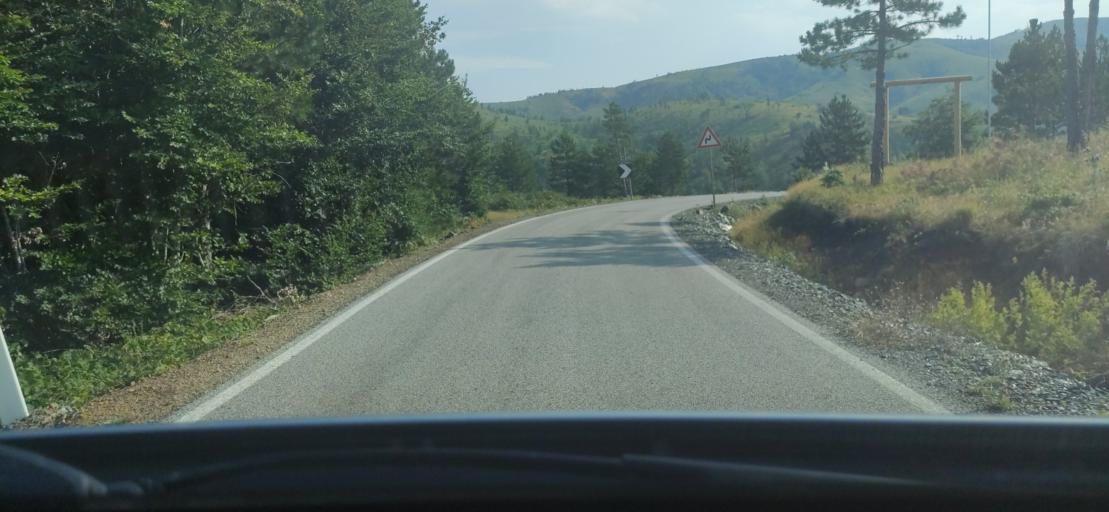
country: AL
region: Shkoder
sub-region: Rrethi i Pukes
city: Iballe
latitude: 42.1729
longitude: 20.0248
